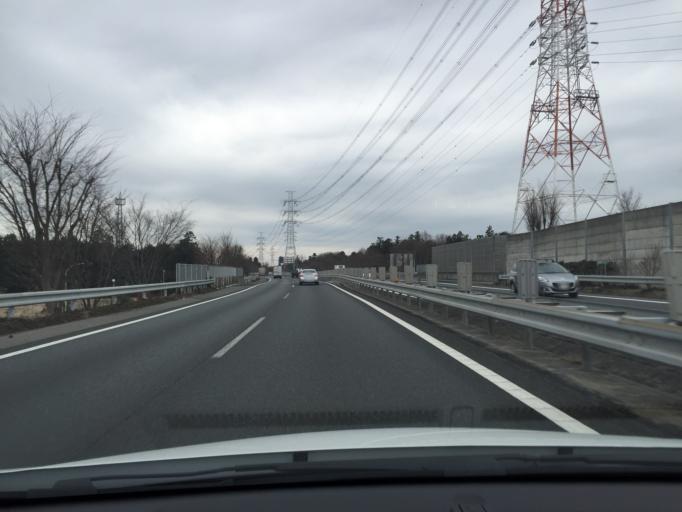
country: JP
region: Saitama
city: Sakado
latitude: 35.9147
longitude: 139.3869
